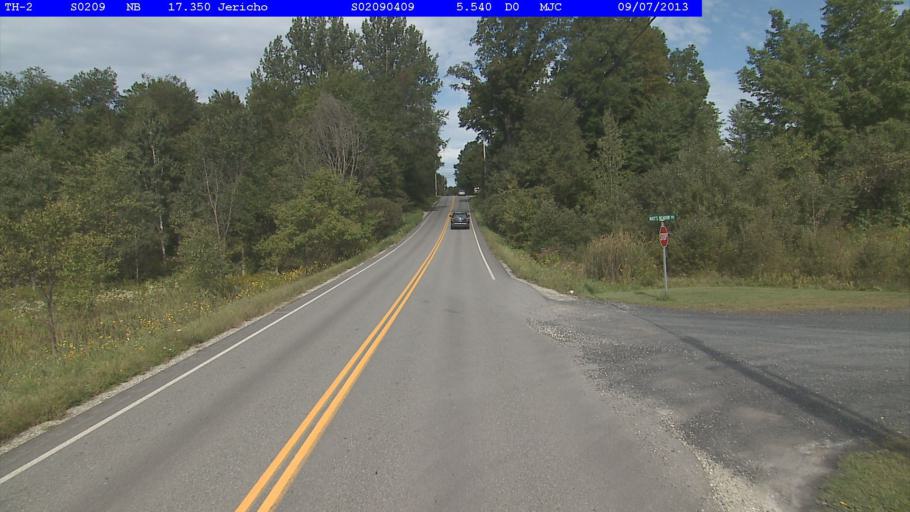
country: US
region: Vermont
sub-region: Chittenden County
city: Jericho
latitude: 44.4997
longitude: -72.9924
